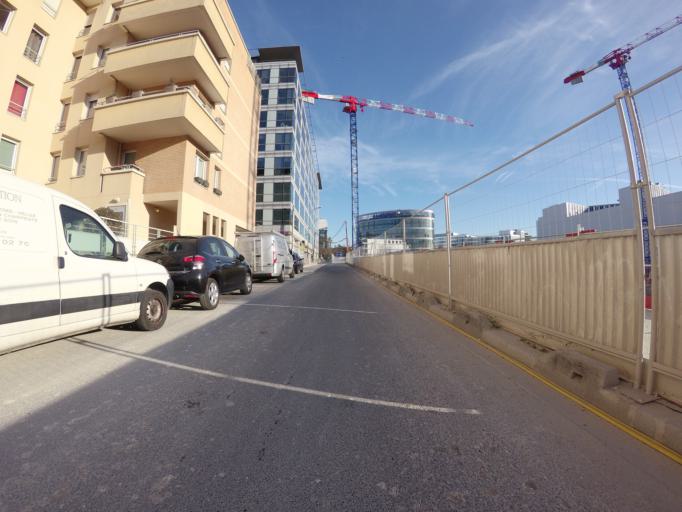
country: FR
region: Ile-de-France
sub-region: Departement des Hauts-de-Seine
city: Clichy
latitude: 48.9027
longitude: 2.3209
